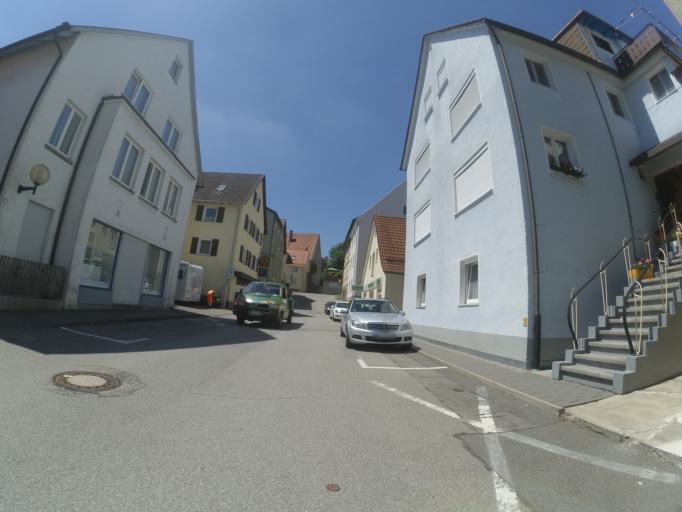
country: DE
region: Baden-Wuerttemberg
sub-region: Tuebingen Region
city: Bad Waldsee
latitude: 47.9225
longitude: 9.7529
